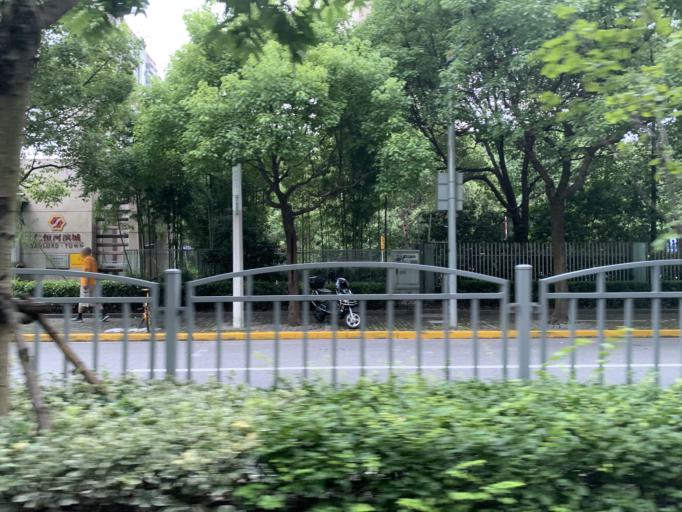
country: CN
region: Shanghai Shi
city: Huamu
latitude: 31.2290
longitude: 121.5617
